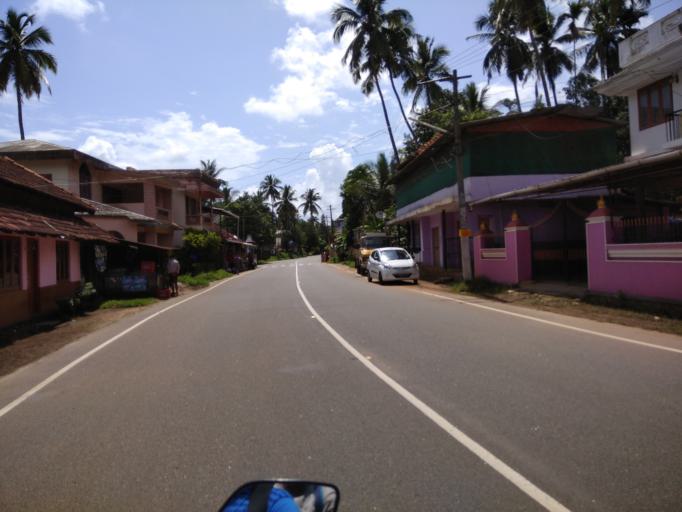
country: IN
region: Kerala
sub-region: Thrissur District
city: Trichur
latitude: 10.5442
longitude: 76.3258
